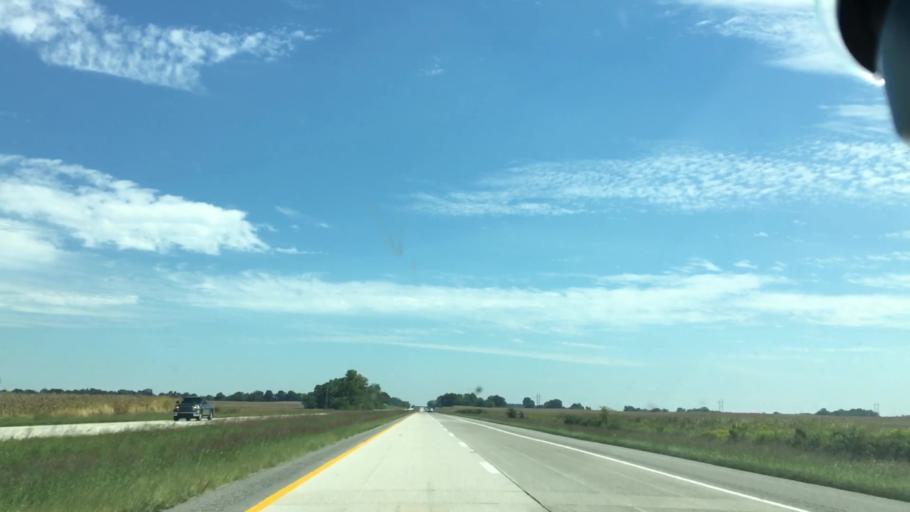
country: US
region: Kentucky
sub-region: Henderson County
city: Henderson
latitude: 37.8017
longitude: -87.5188
